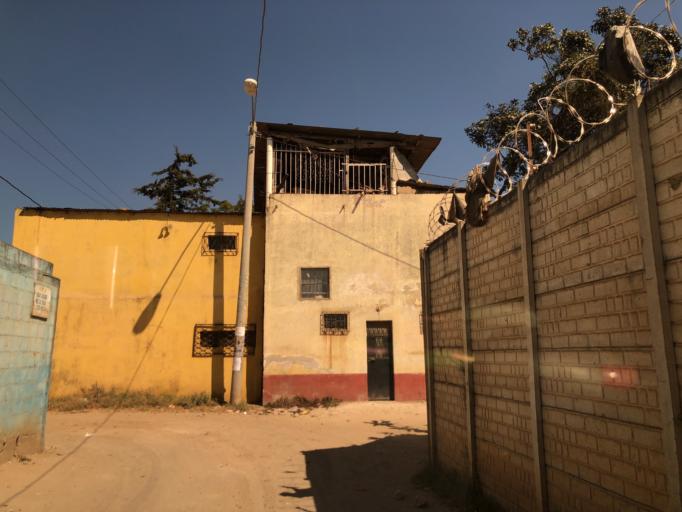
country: GT
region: Guatemala
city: Mixco
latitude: 14.6197
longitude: -90.5805
